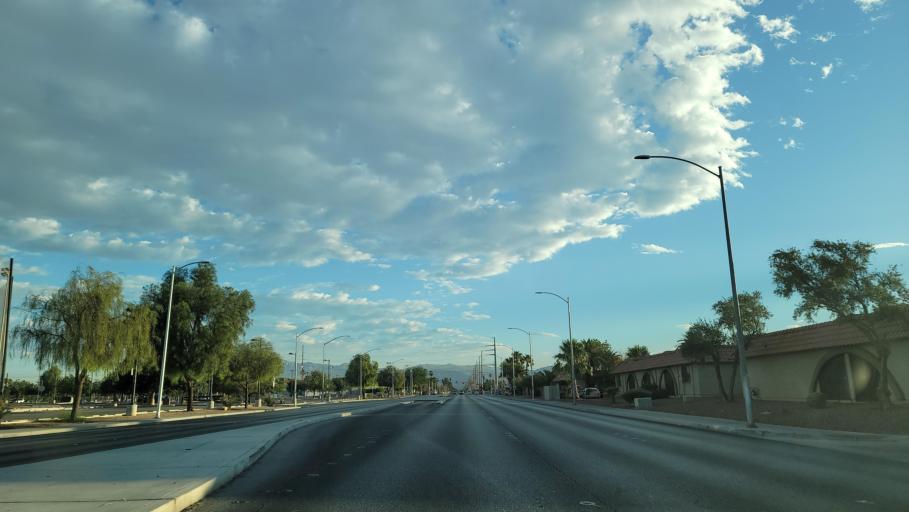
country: US
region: Nevada
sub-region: Clark County
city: North Las Vegas
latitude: 36.1778
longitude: -115.0983
